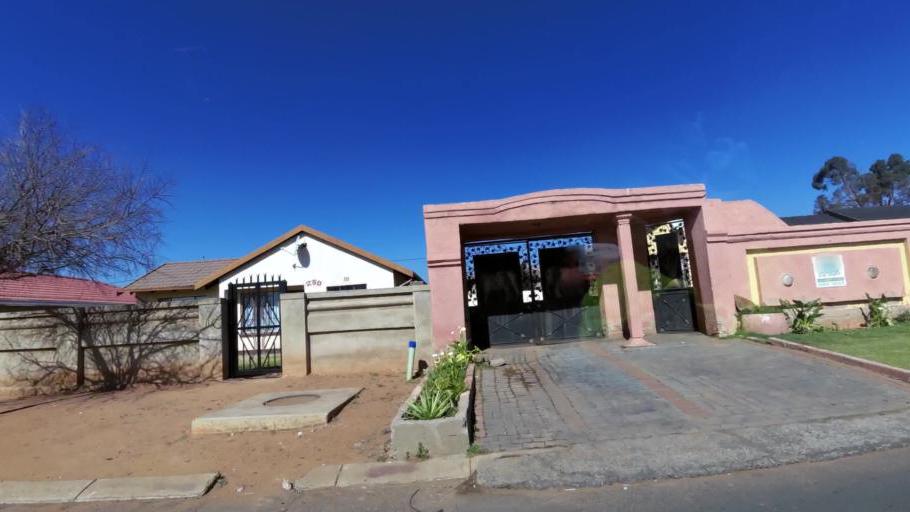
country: ZA
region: Gauteng
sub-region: City of Johannesburg Metropolitan Municipality
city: Johannesburg
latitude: -26.2498
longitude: 27.9813
